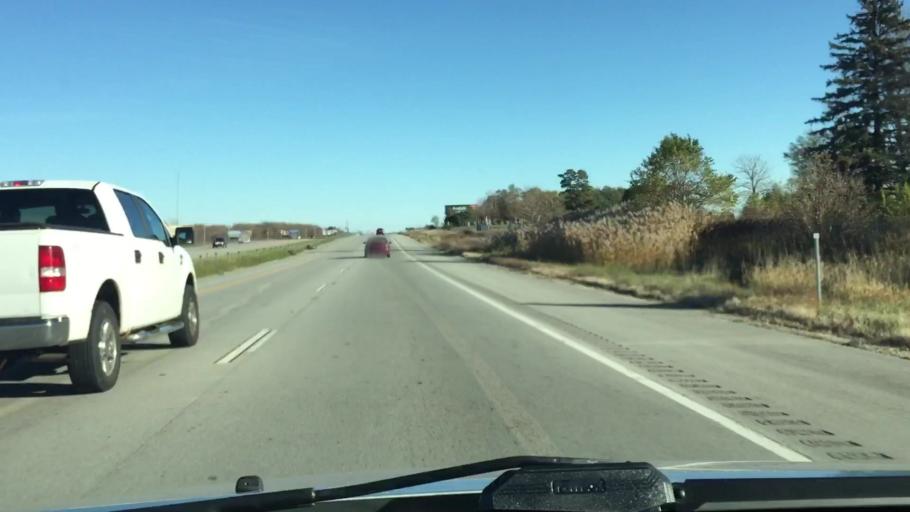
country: US
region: Wisconsin
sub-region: Brown County
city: Wrightstown
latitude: 44.3340
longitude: -88.2058
